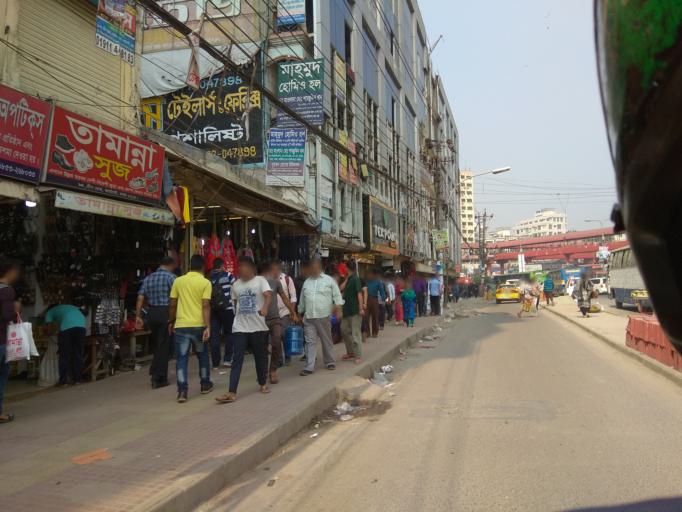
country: BD
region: Dhaka
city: Azimpur
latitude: 23.7573
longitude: 90.3899
